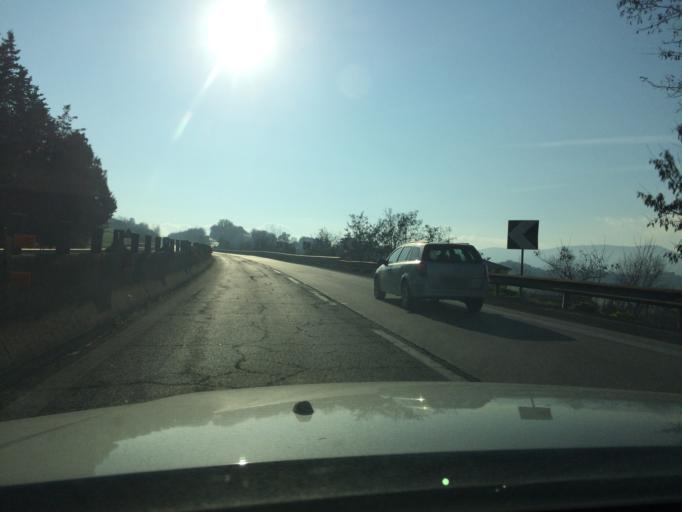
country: IT
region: Umbria
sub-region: Provincia di Perugia
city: Ponterio-Pian di Porto
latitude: 42.8317
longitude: 12.4006
